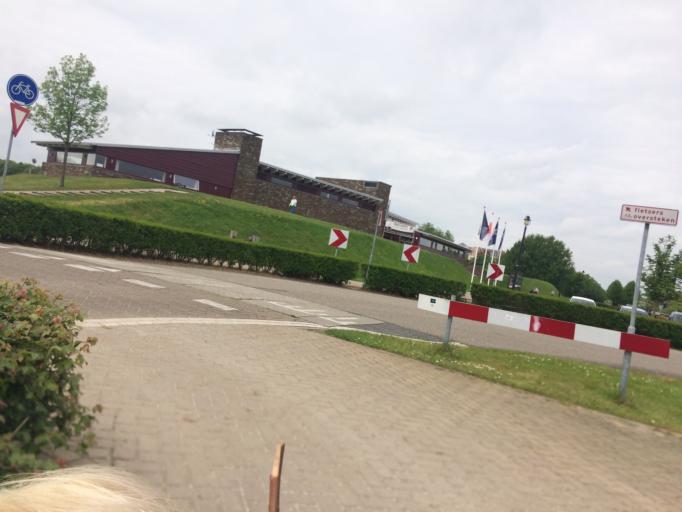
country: NL
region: Gelderland
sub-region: Gemeente Maasdriel
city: Hedel
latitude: 51.7245
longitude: 5.2563
